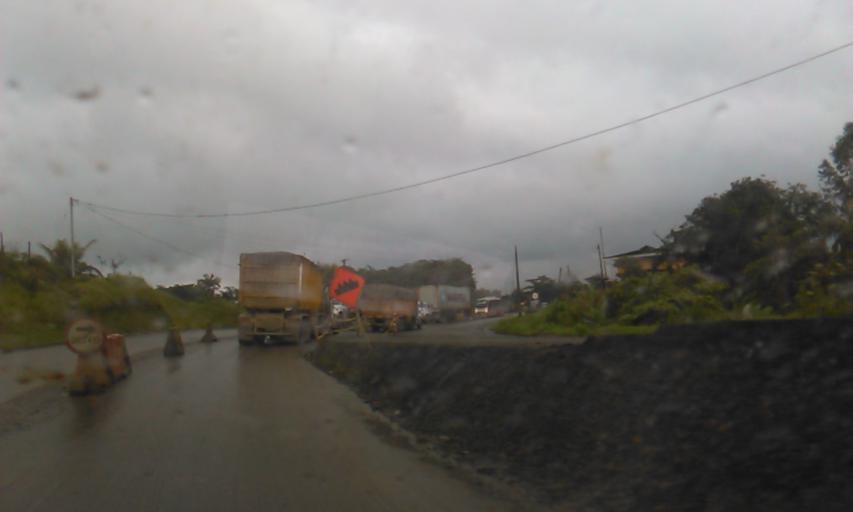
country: CO
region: Valle del Cauca
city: Buenaventura
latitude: 3.8791
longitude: -76.8973
